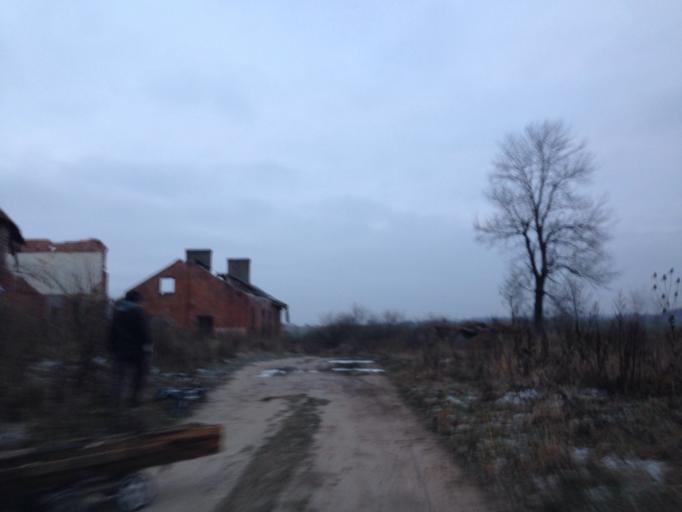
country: PL
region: Warmian-Masurian Voivodeship
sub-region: Powiat ketrzynski
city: Ketrzyn
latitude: 54.0434
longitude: 21.3073
